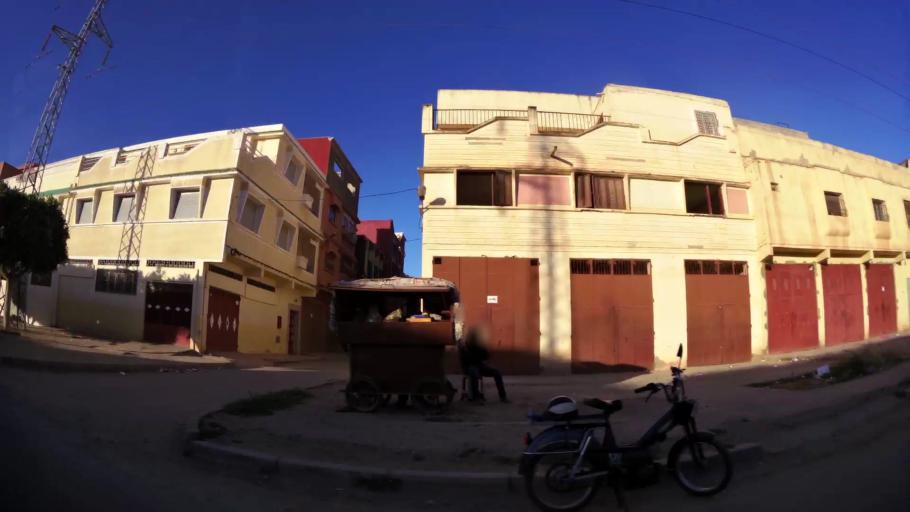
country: MA
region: Oriental
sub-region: Berkane-Taourirt
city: Berkane
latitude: 34.9233
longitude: -2.3123
